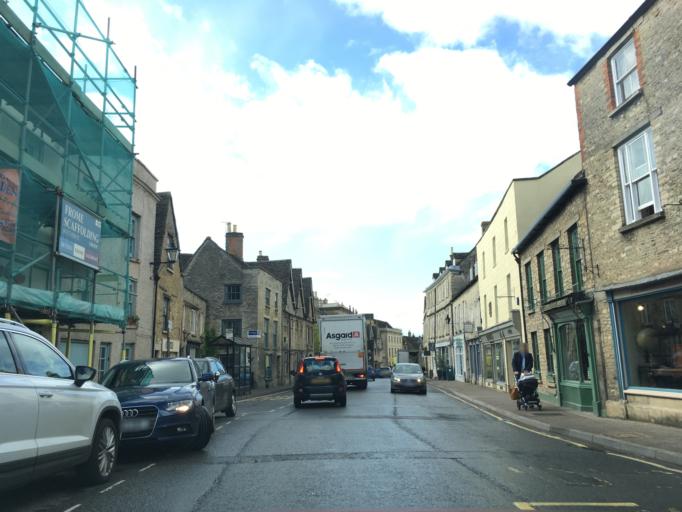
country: GB
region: England
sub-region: Gloucestershire
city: Tetbury
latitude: 51.6375
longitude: -2.1605
